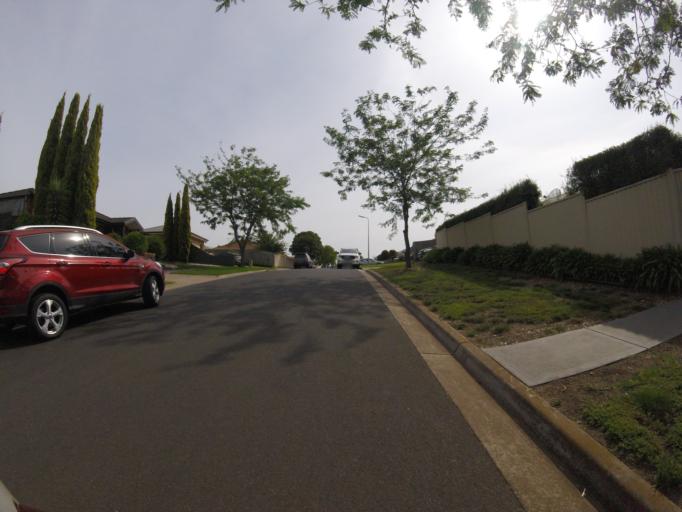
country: AU
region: Victoria
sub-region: Hume
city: Meadow Heights
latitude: -37.6500
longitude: 144.9023
